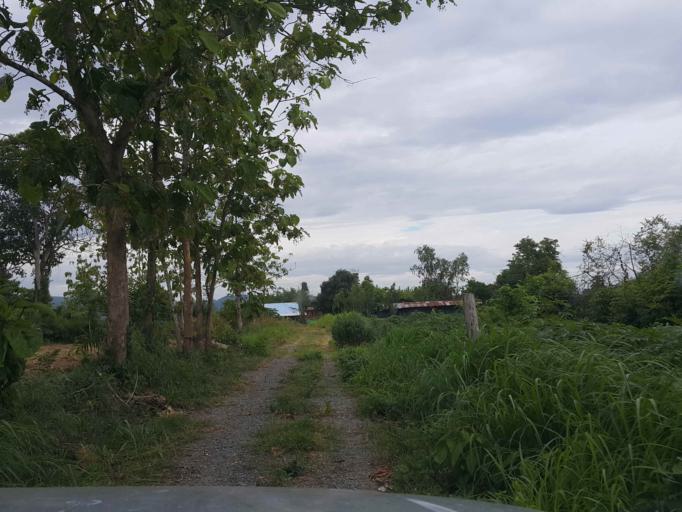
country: TH
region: Sukhothai
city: Thung Saliam
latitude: 17.3234
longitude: 99.4460
